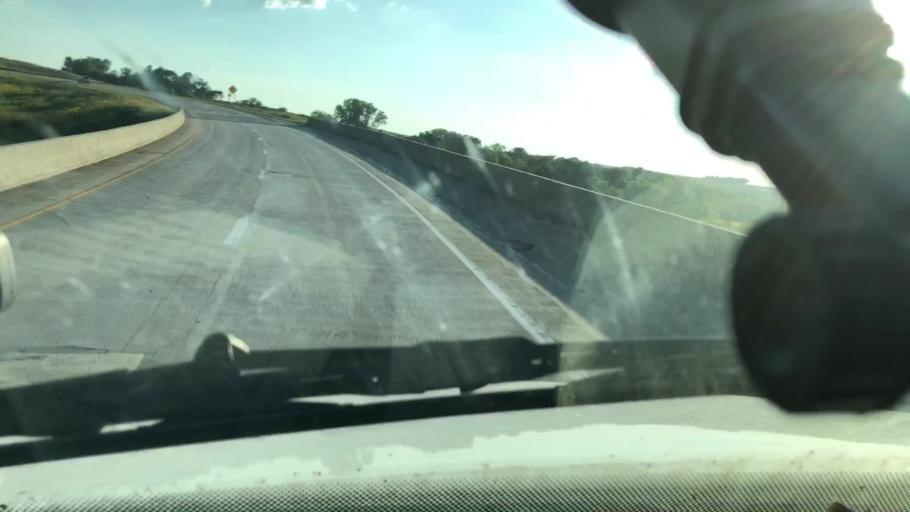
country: US
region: Iowa
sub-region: Pottawattamie County
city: Avoca
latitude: 41.4972
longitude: -95.5842
